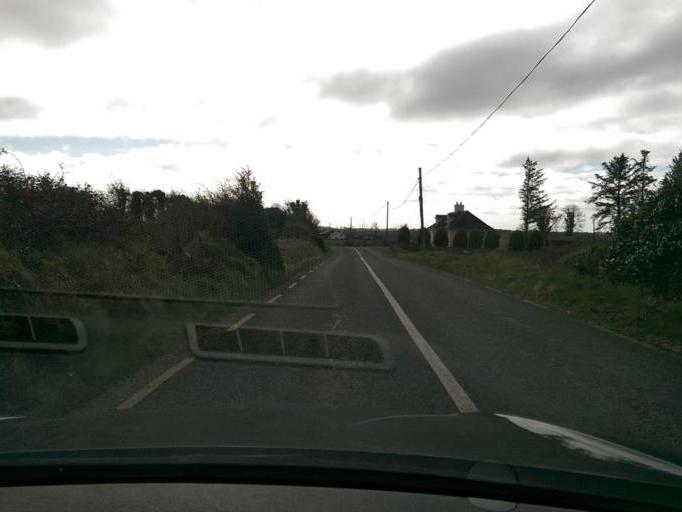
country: IE
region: Connaught
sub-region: County Galway
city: Ballinasloe
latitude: 53.4337
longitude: -8.4274
